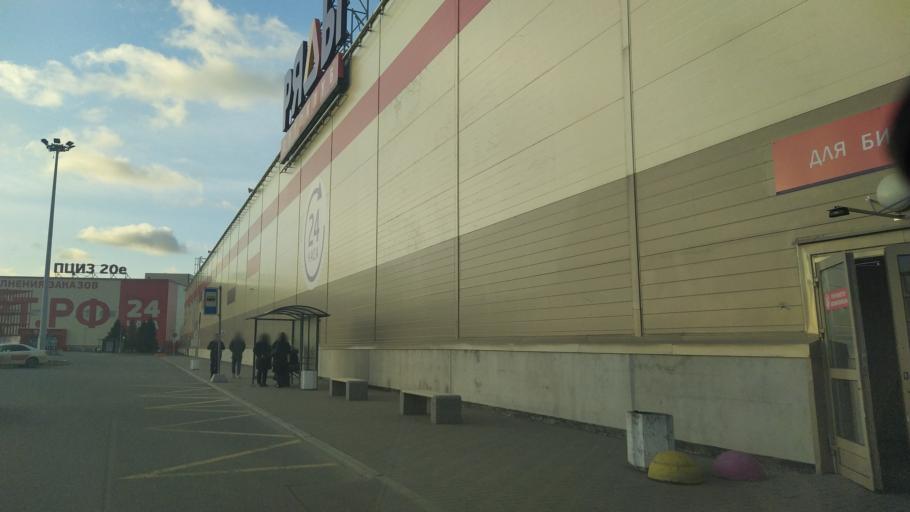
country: RU
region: St.-Petersburg
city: Aleksandrovskaya
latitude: 59.7879
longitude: 30.3220
